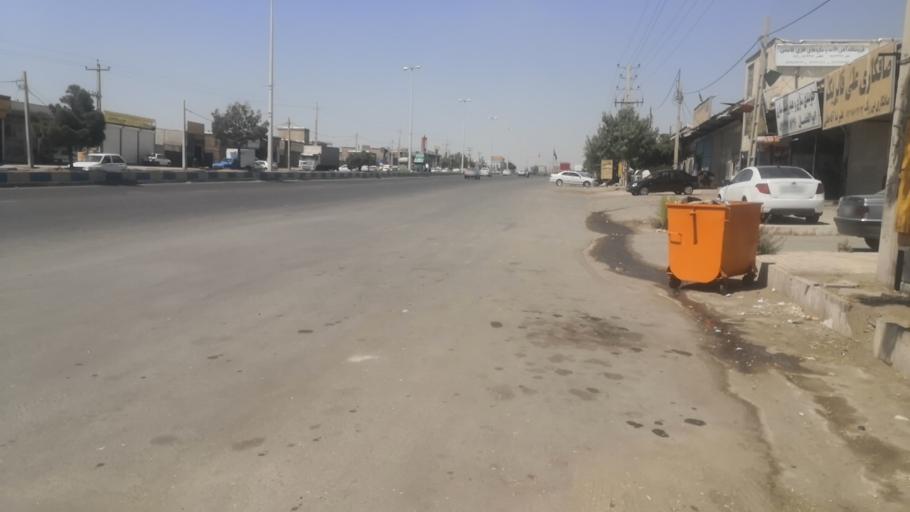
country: IR
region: Qazvin
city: Abyek
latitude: 36.0291
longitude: 50.5454
